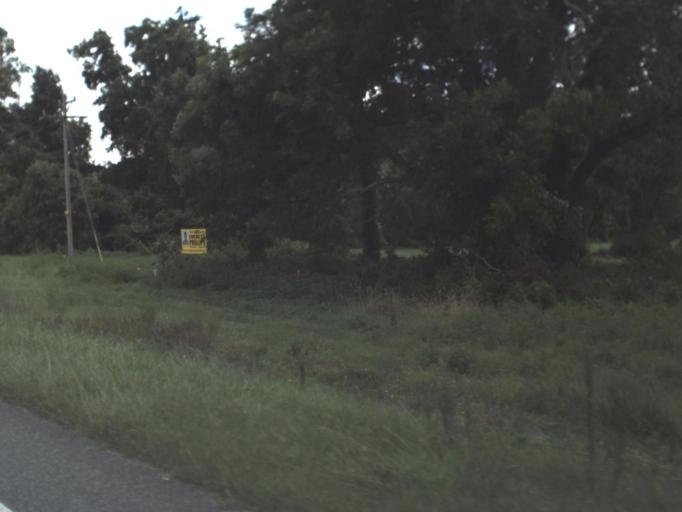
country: US
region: Florida
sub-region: Alachua County
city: High Springs
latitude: 30.0041
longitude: -82.5974
